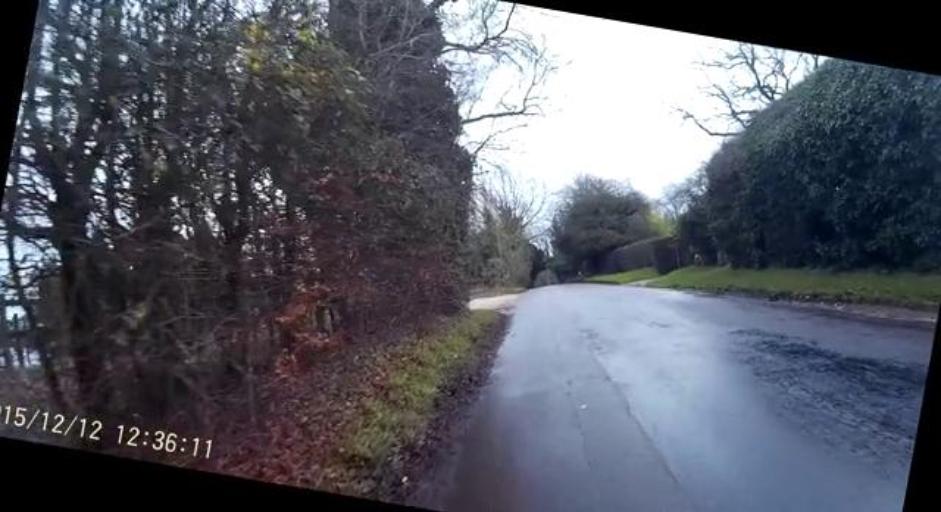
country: GB
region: England
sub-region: Hampshire
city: Cowplain
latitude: 50.9529
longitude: -0.9832
